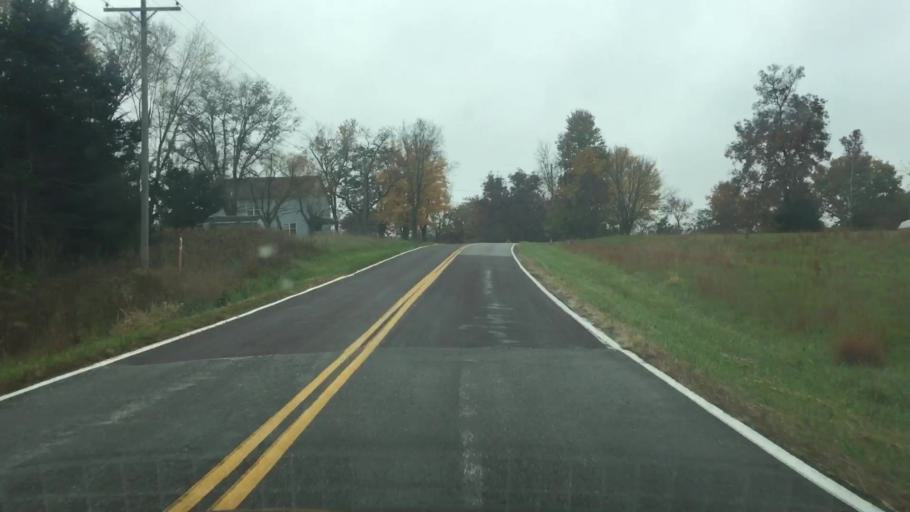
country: US
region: Missouri
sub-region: Callaway County
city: Fulton
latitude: 38.8229
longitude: -91.9084
